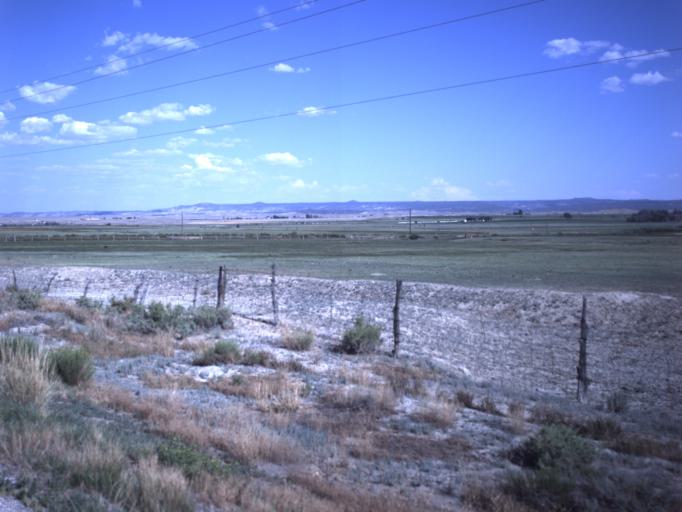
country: US
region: Utah
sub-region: Emery County
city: Huntington
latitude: 39.3472
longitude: -110.8740
